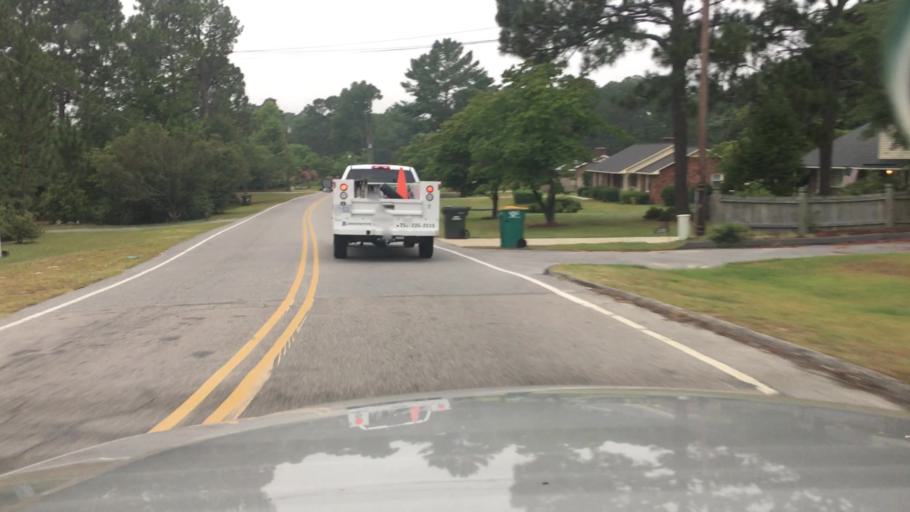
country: US
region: North Carolina
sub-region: Cumberland County
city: Hope Mills
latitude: 34.9750
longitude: -78.9393
